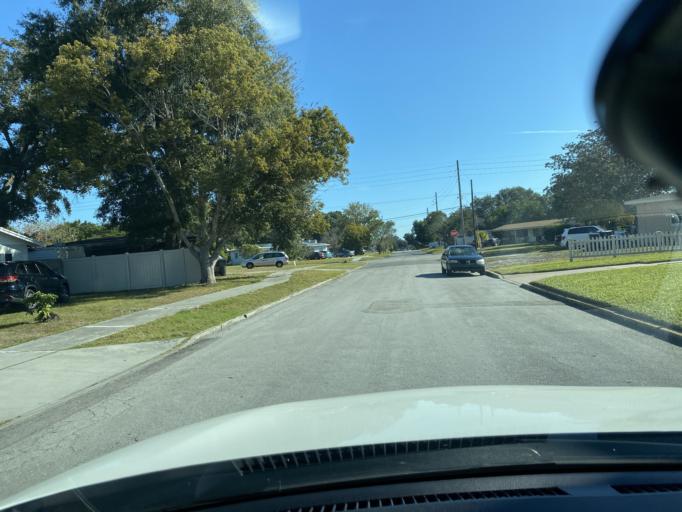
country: US
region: Florida
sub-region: Orange County
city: Azalea Park
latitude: 28.5276
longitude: -81.3158
